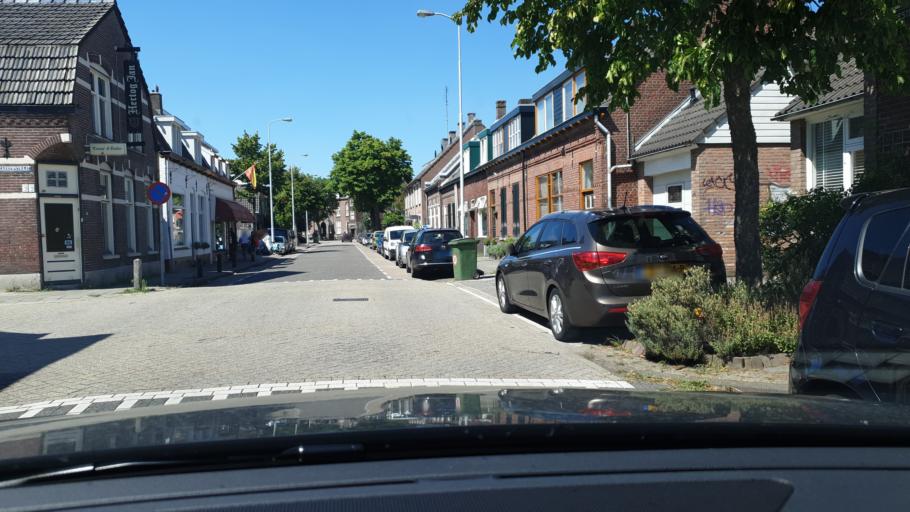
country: NL
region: North Brabant
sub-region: Gemeente Eindhoven
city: Eindhoven
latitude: 51.4395
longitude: 5.4584
